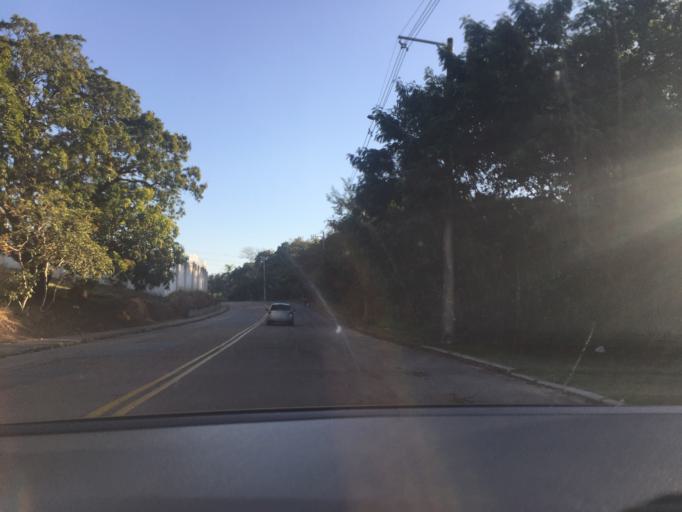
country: BR
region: Sao Paulo
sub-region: Louveira
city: Louveira
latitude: -23.1203
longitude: -46.9260
